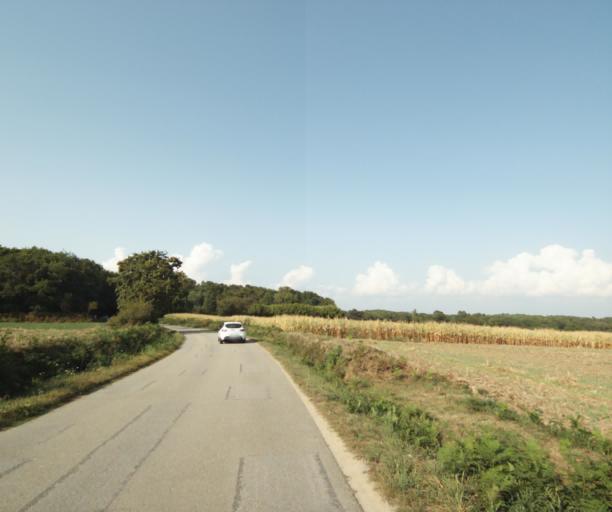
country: FR
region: Brittany
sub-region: Departement du Morbihan
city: Riantec
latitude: 47.7332
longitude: -3.2957
